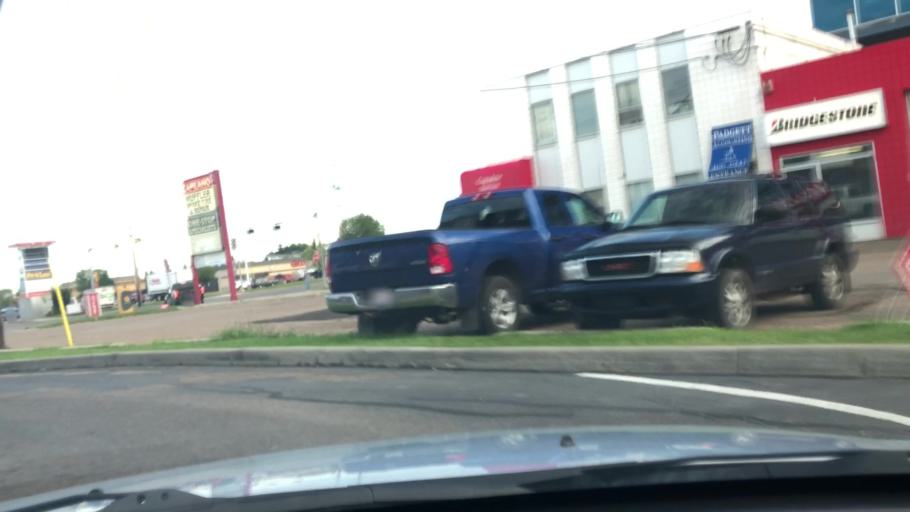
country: CA
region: Alberta
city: Edmonton
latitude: 53.5392
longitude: -113.4174
